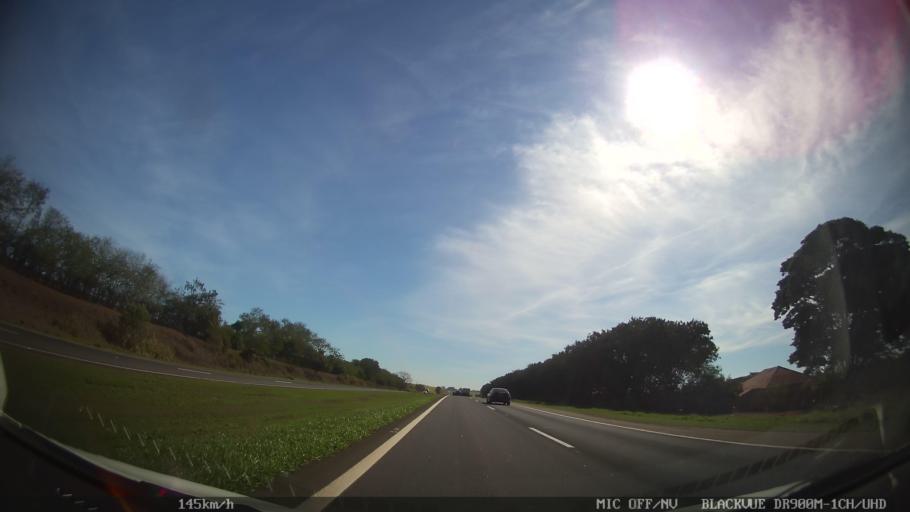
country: BR
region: Sao Paulo
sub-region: Leme
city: Leme
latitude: -22.1248
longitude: -47.4103
